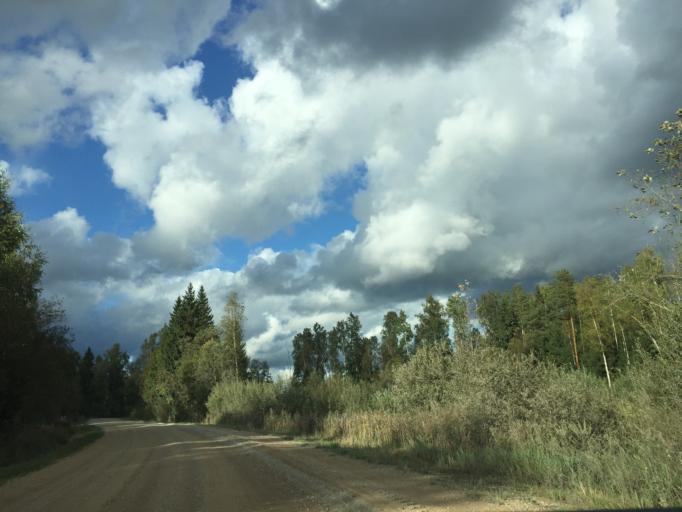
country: LV
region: Malpils
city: Malpils
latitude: 57.0229
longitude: 25.0508
